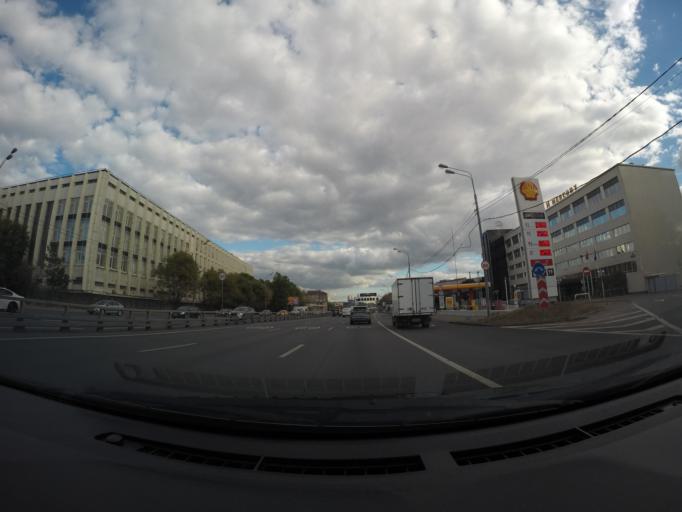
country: RU
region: Moscow
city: Sokol'niki
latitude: 55.7922
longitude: 37.6544
